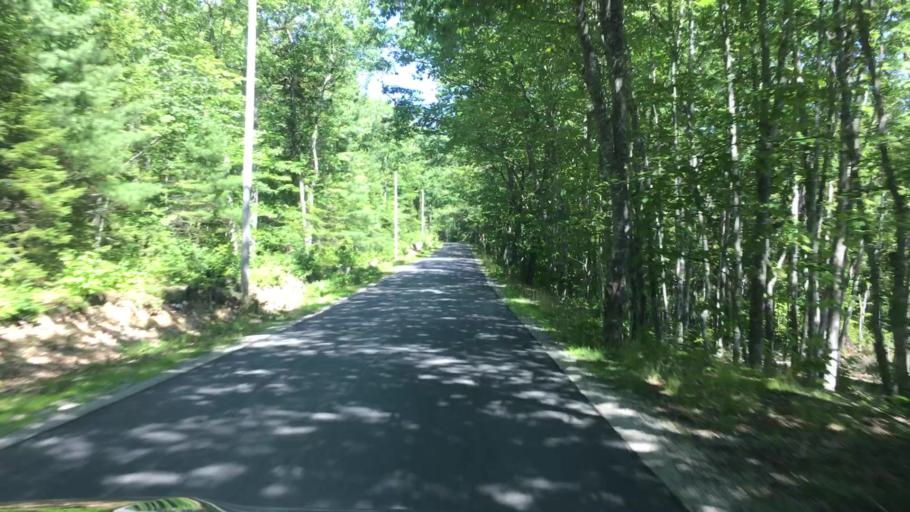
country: US
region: Maine
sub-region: Hancock County
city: Sedgwick
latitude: 44.3345
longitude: -68.6608
